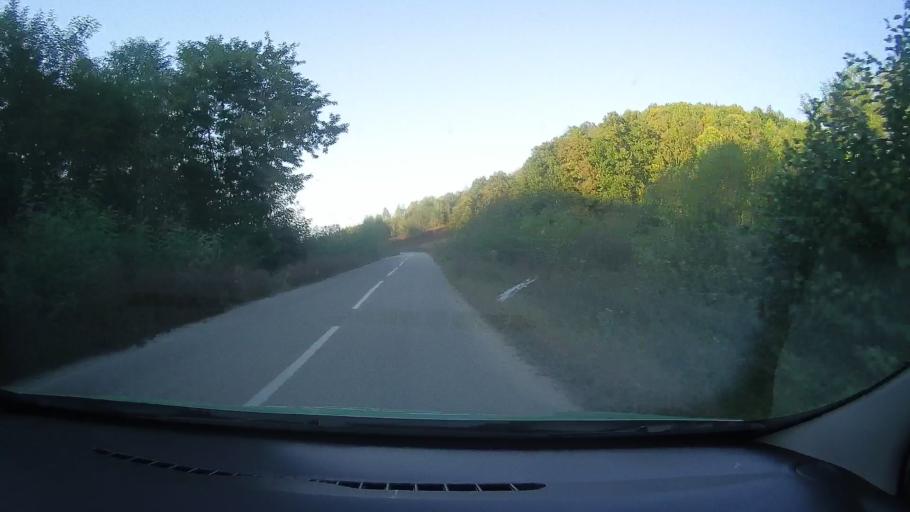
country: RO
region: Timis
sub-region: Comuna Fardea
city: Fardea
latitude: 45.6958
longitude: 22.1599
